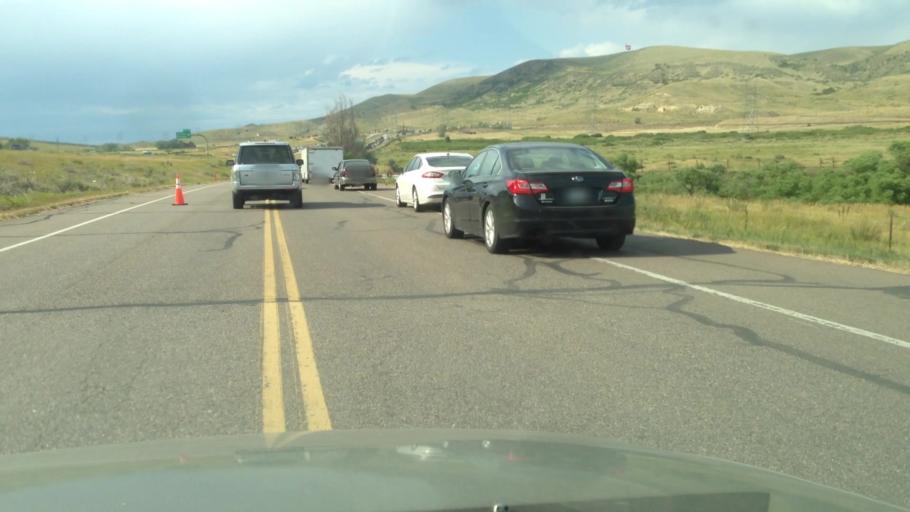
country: US
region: Colorado
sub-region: Jefferson County
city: West Pleasant View
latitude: 39.6761
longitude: -105.1881
